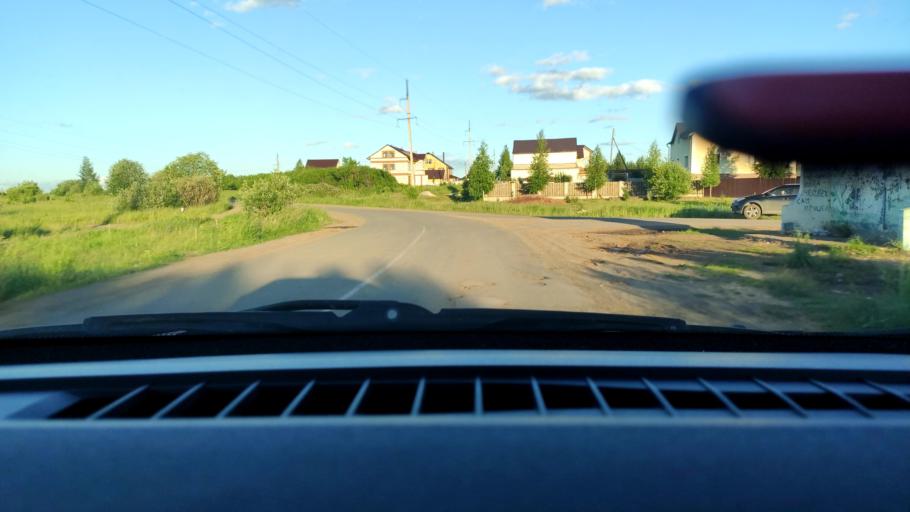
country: RU
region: Perm
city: Kultayevo
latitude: 57.9295
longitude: 55.8630
